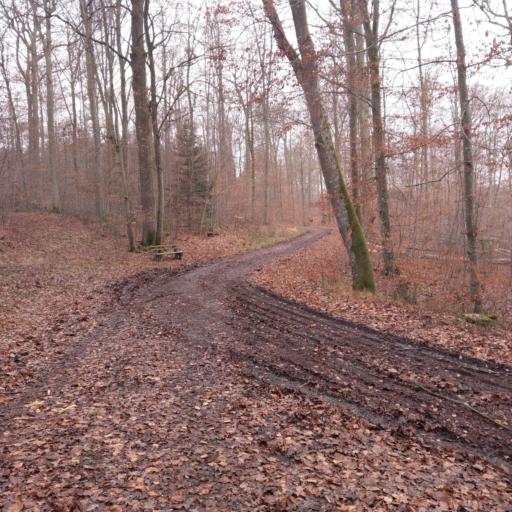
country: DE
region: Baden-Wuerttemberg
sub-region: Tuebingen Region
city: Dettenhausen
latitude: 48.6269
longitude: 9.1062
